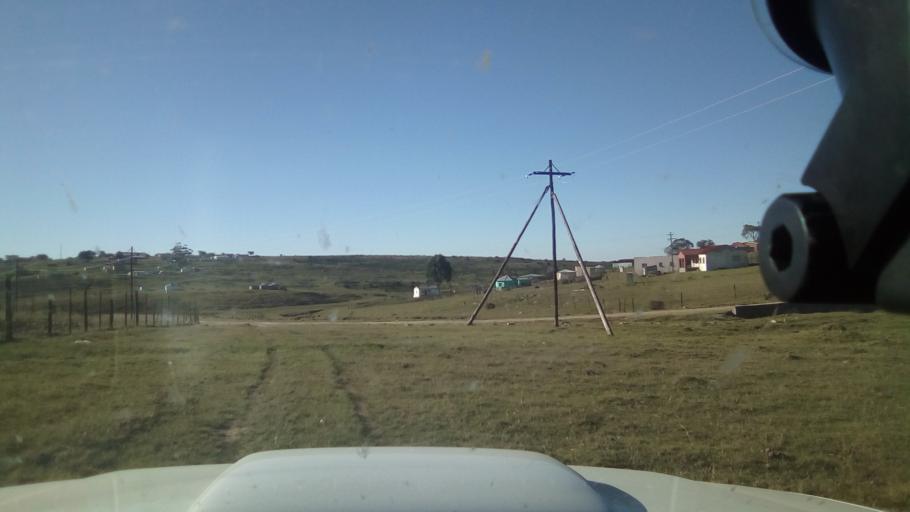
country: ZA
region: Eastern Cape
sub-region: Buffalo City Metropolitan Municipality
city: Bhisho
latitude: -32.9477
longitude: 27.2895
